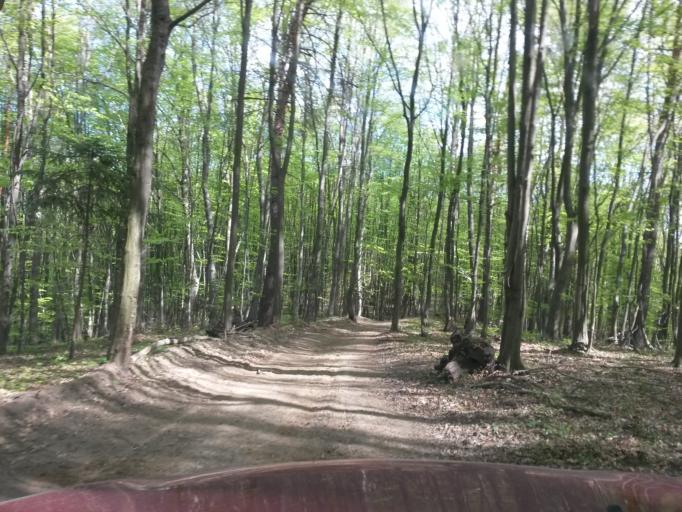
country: SK
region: Presovsky
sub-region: Okres Presov
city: Presov
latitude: 48.9524
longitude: 21.1335
